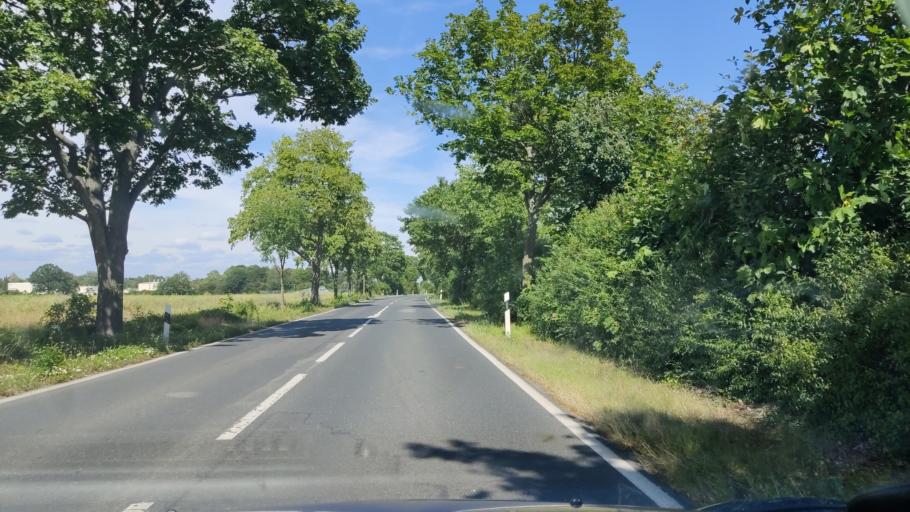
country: DE
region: Lower Saxony
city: Ronnenberg
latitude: 52.3352
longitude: 9.6451
